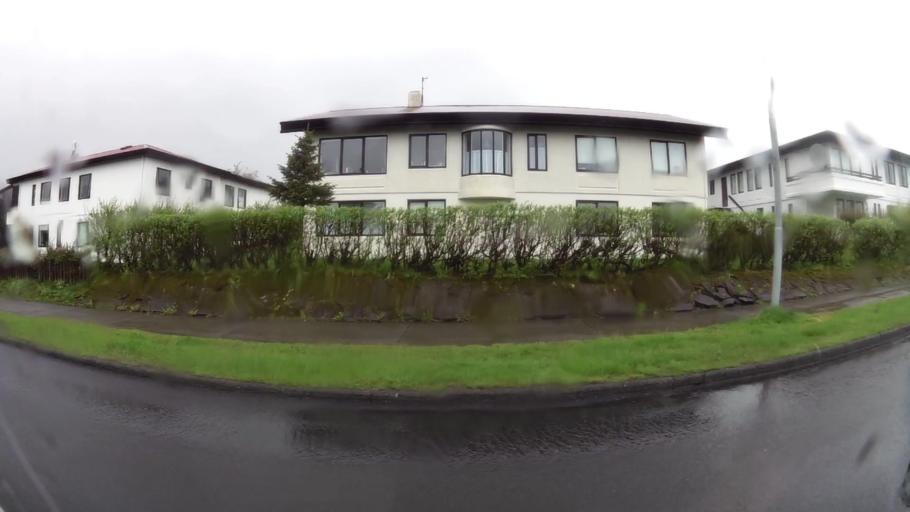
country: IS
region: Capital Region
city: Reykjavik
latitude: 64.0933
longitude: -21.8405
